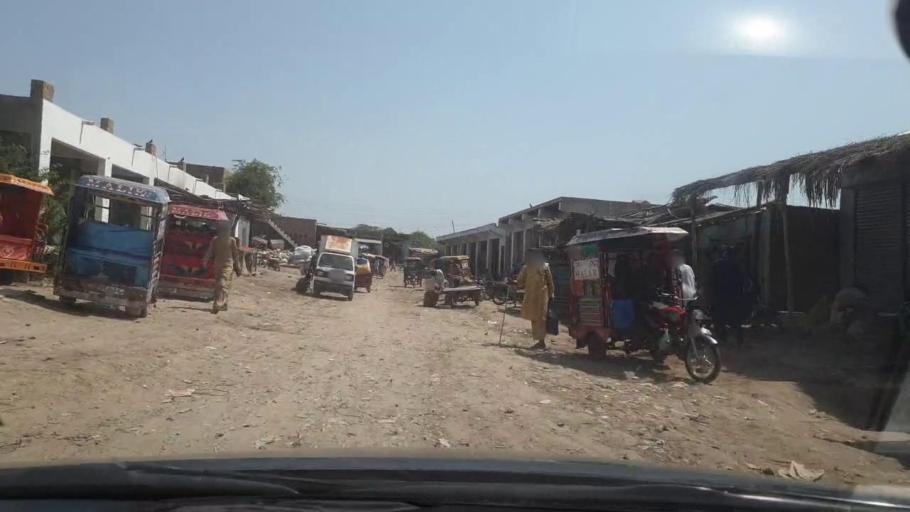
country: PK
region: Sindh
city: Naukot
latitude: 24.7666
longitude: 69.1974
